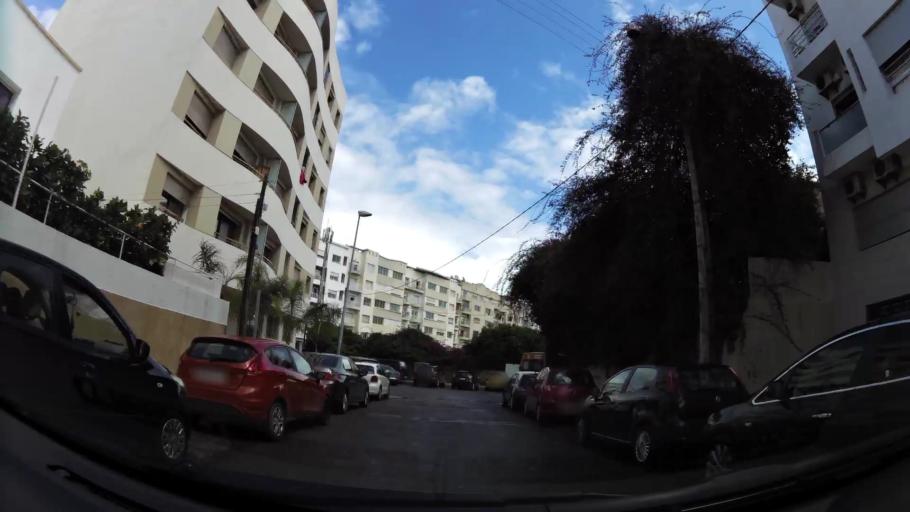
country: MA
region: Grand Casablanca
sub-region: Casablanca
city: Casablanca
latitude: 33.5734
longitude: -7.6364
